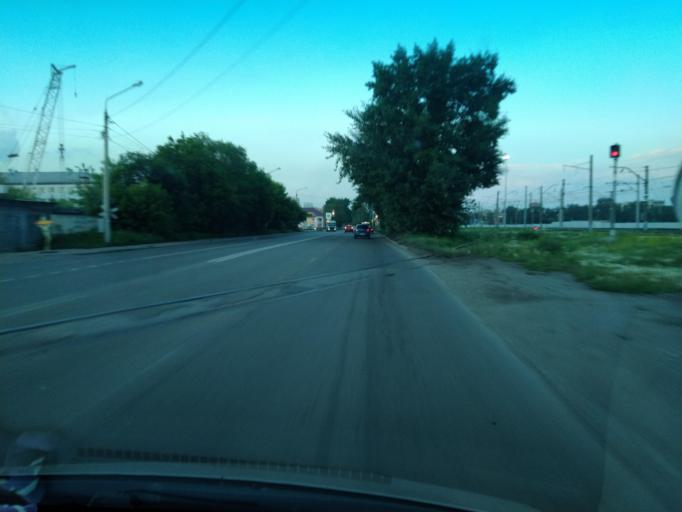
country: RU
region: Krasnoyarskiy
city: Krasnoyarsk
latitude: 55.9923
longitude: 92.9228
